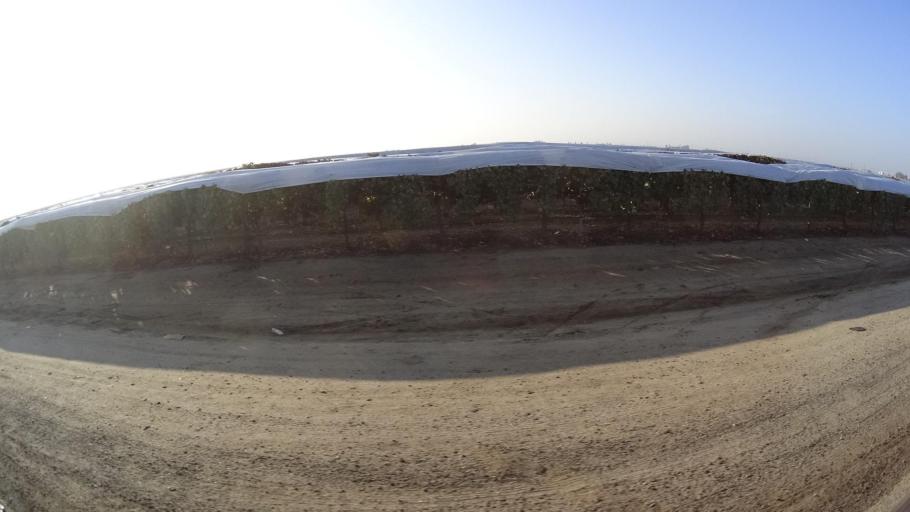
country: US
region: California
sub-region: Tulare County
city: Richgrove
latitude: 35.7906
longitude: -119.1726
